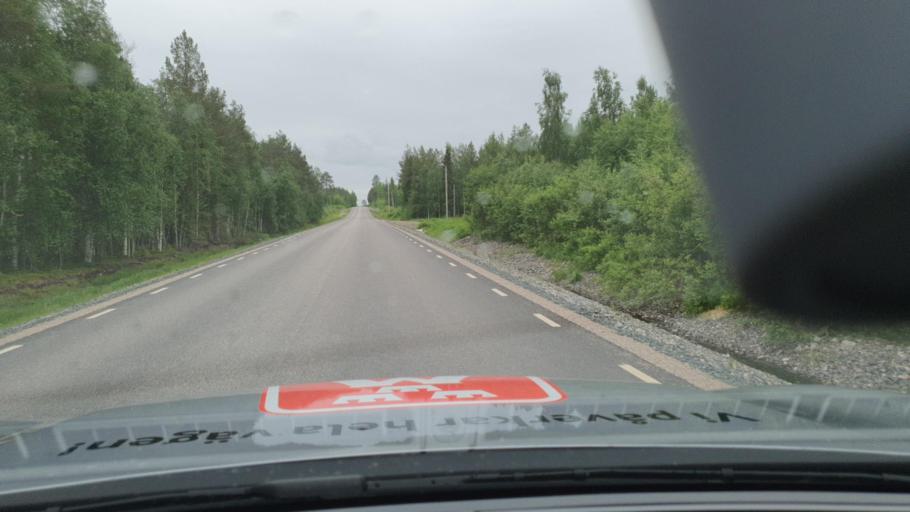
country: SE
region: Norrbotten
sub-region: Overtornea Kommun
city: OEvertornea
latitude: 66.5780
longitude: 23.3307
